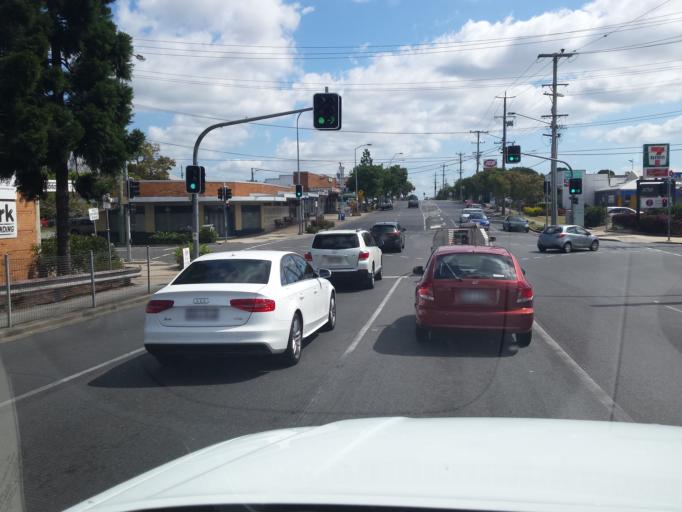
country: AU
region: Queensland
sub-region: Brisbane
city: Zillmere
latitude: -27.3598
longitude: 153.0382
